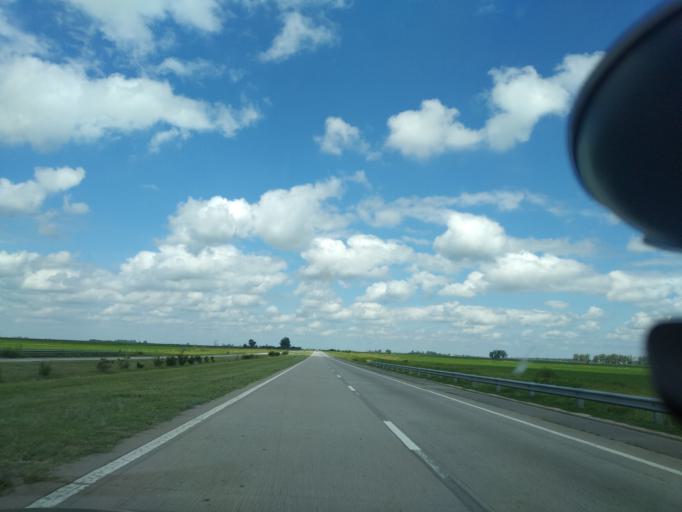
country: AR
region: Cordoba
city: Leones
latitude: -32.6150
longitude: -62.3788
